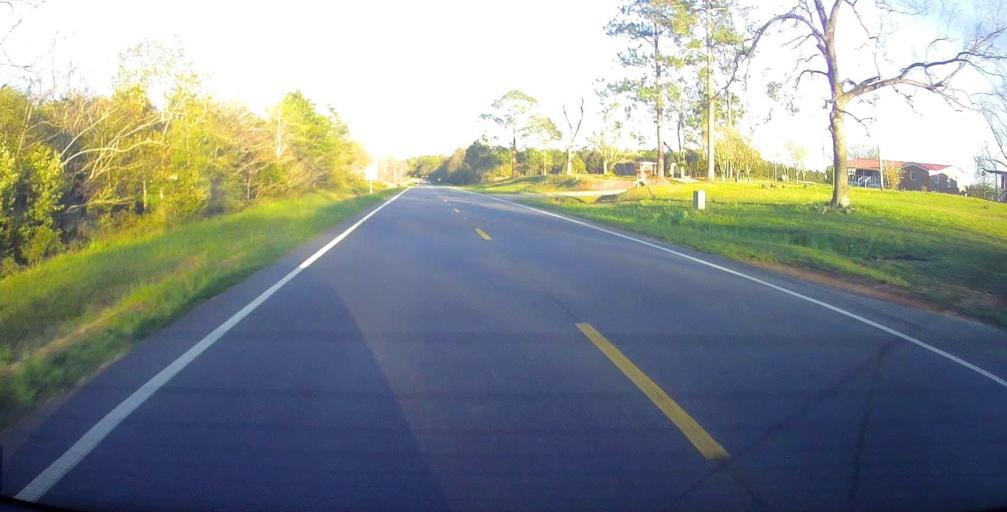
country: US
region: Georgia
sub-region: Wilcox County
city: Rochelle
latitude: 31.9453
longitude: -83.5224
